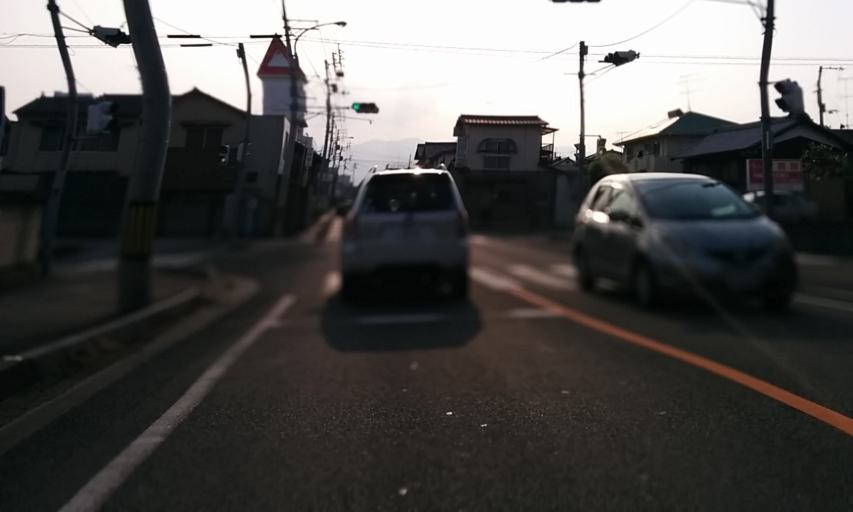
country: JP
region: Ehime
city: Saijo
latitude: 33.8969
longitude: 133.1189
